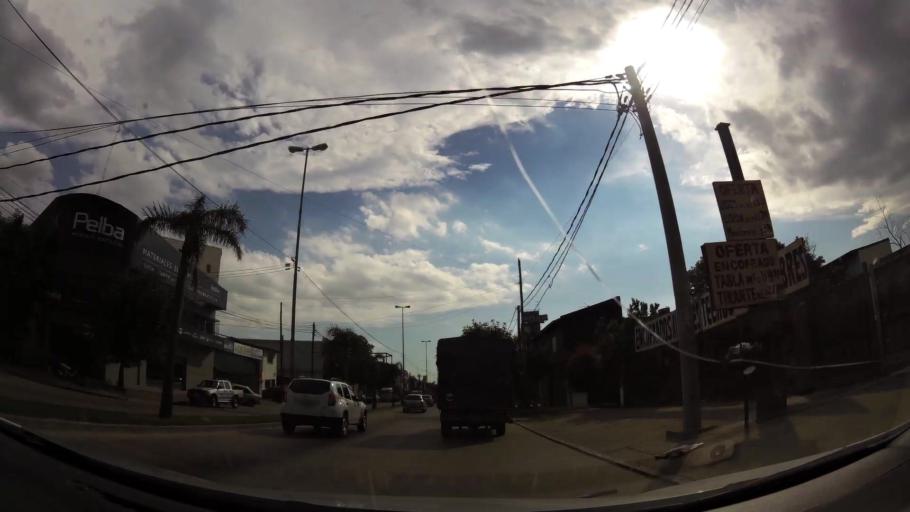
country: AR
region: Buenos Aires
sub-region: Partido de Tigre
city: Tigre
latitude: -34.4834
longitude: -58.6112
